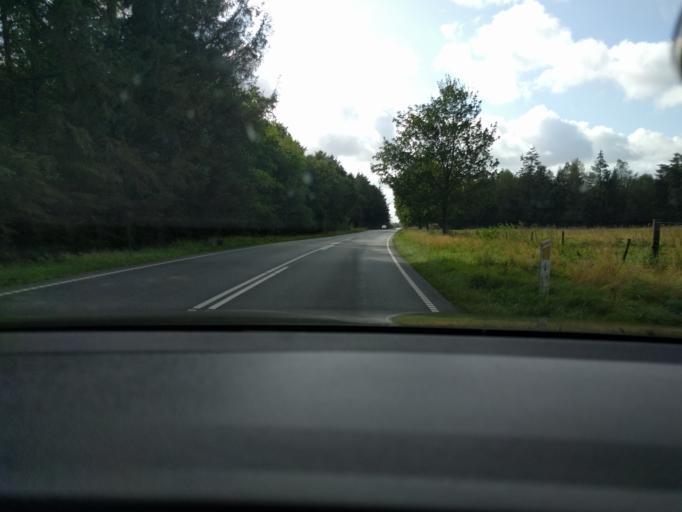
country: DK
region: Central Jutland
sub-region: Viborg Kommune
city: Bjerringbro
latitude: 56.2847
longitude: 9.6473
